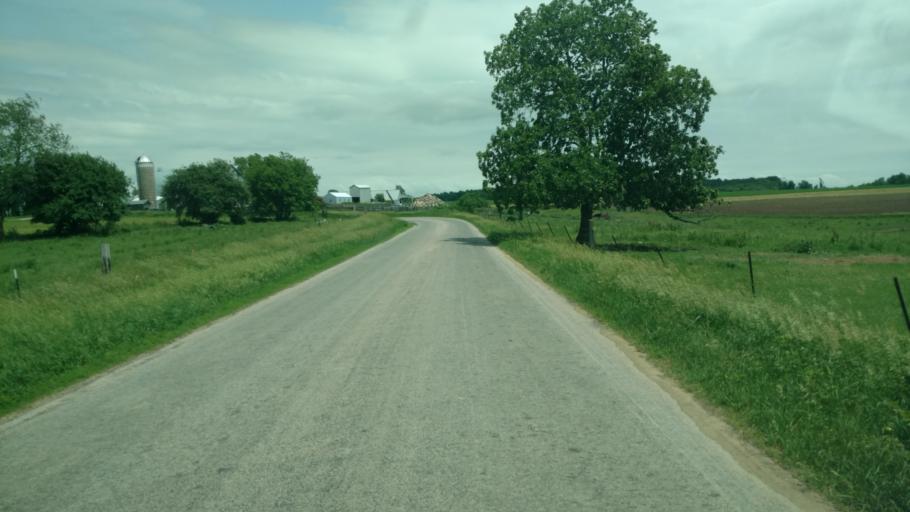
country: US
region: Wisconsin
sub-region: Monroe County
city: Cashton
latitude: 43.6885
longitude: -90.6721
